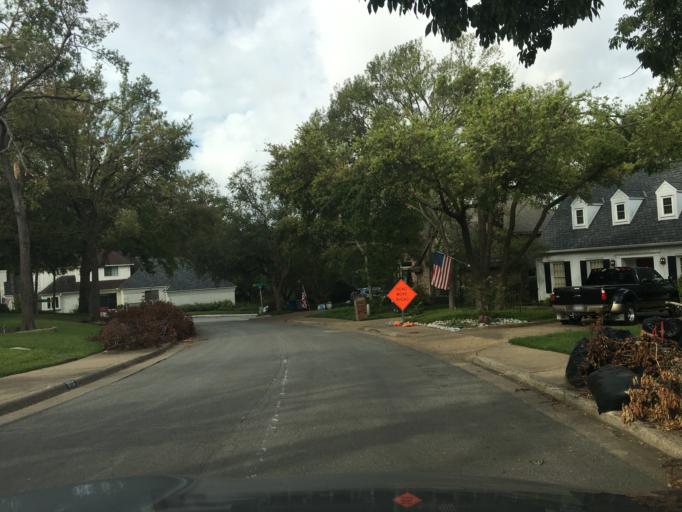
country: US
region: Texas
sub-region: Dallas County
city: Richardson
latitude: 32.8997
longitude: -96.7494
